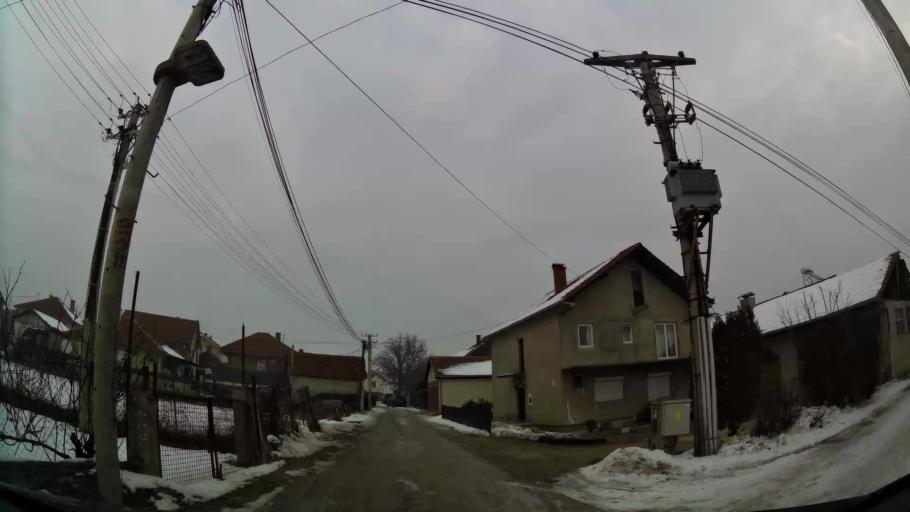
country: MK
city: Kondovo
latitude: 42.0467
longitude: 21.3517
